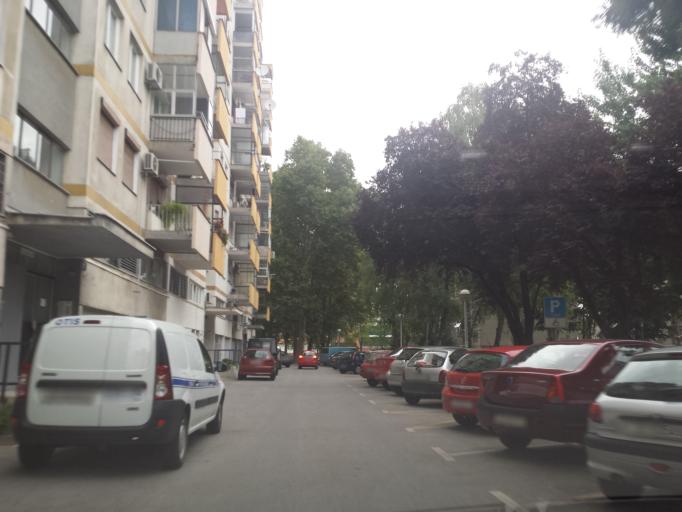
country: HR
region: Grad Zagreb
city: Novi Zagreb
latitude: 45.7919
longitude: 15.9496
